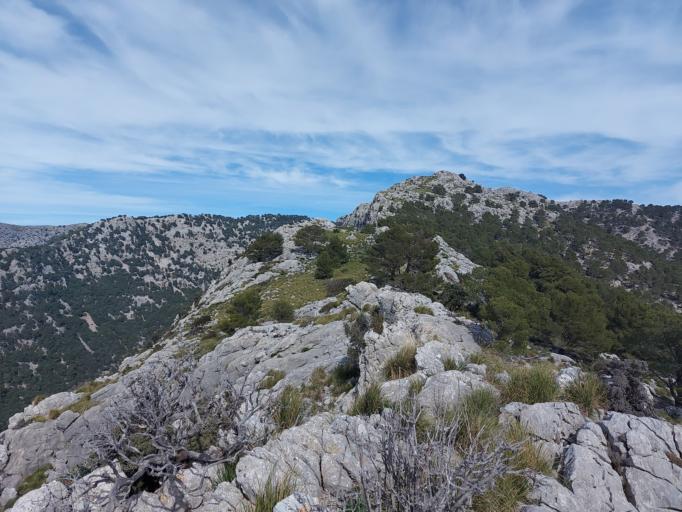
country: ES
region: Balearic Islands
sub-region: Illes Balears
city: Valldemossa
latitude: 39.7073
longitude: 2.6572
